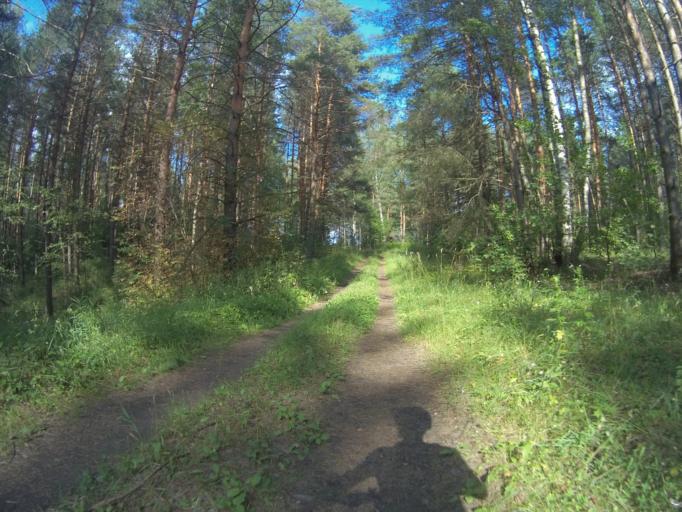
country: RU
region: Vladimir
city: Vorsha
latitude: 56.0092
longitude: 40.1958
